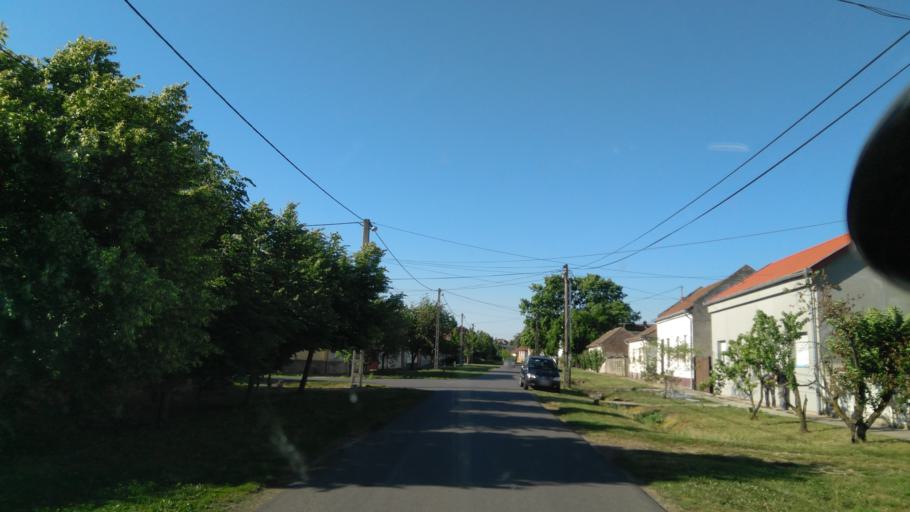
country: HU
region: Bekes
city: Elek
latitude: 46.5316
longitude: 21.2561
